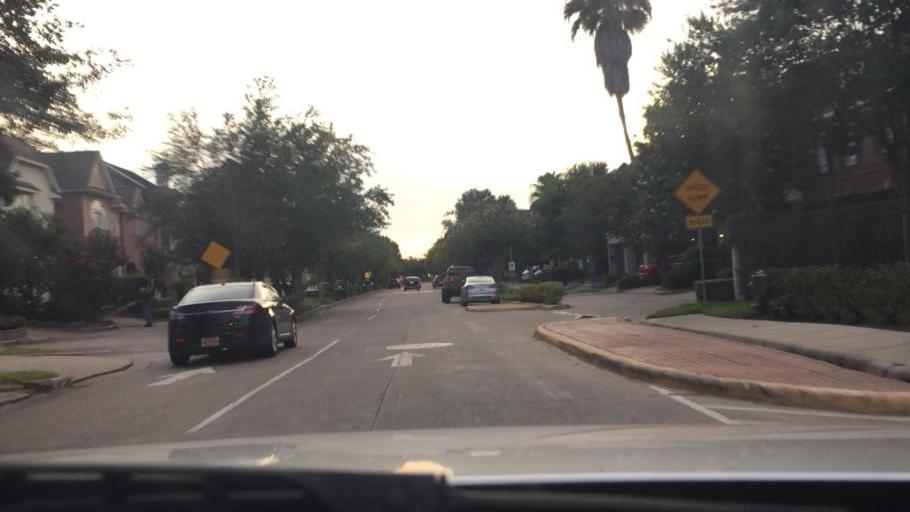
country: US
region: Texas
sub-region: Harris County
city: Bellaire
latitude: 29.7353
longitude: -95.4685
